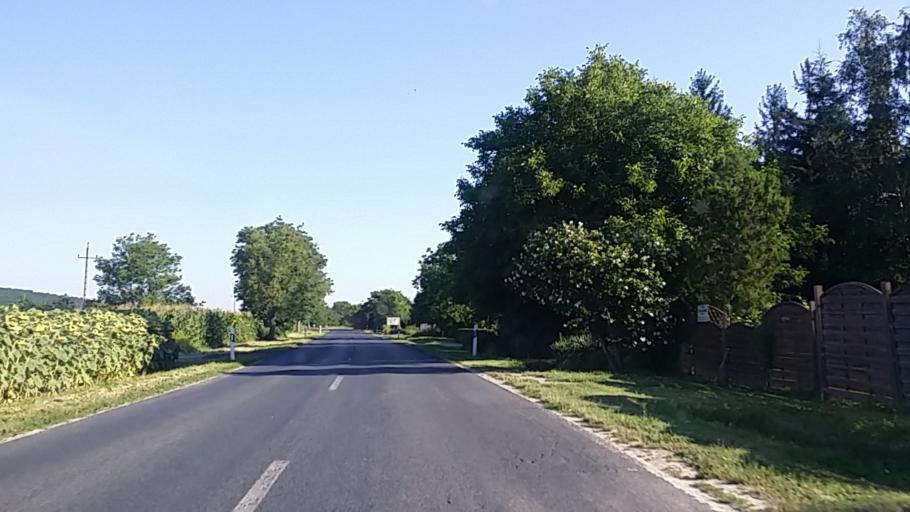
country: HU
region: Zala
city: Cserszegtomaj
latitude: 46.8123
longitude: 17.2029
